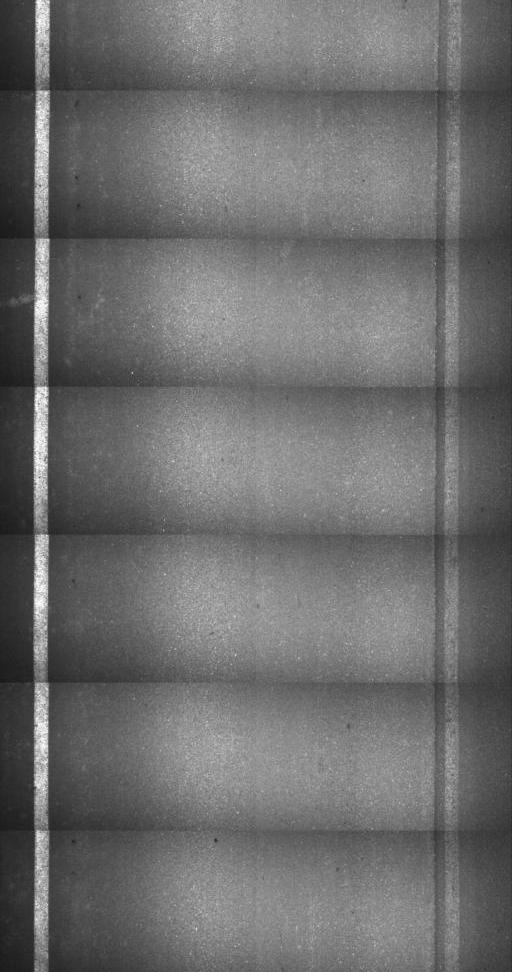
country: US
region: New Hampshire
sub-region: Coos County
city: Colebrook
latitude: 44.9289
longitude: -71.5235
